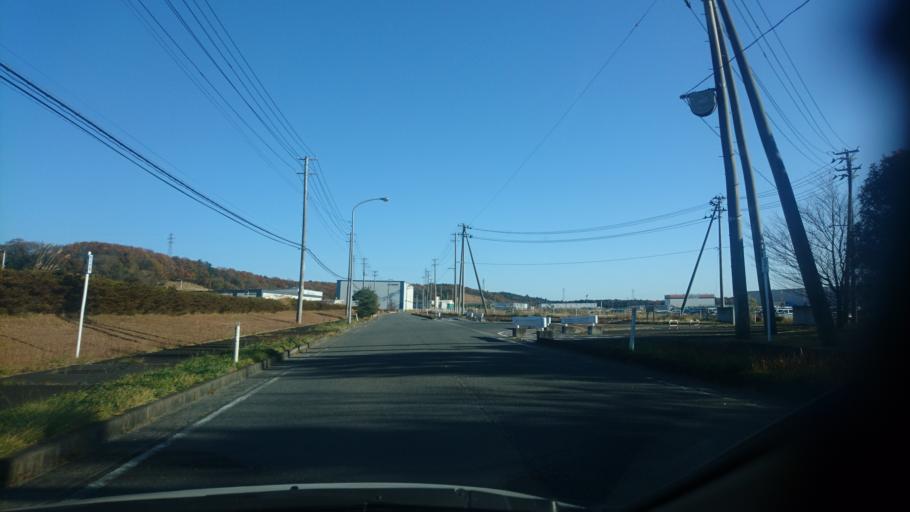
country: JP
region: Miyagi
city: Tomiya
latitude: 38.4637
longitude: 140.9288
